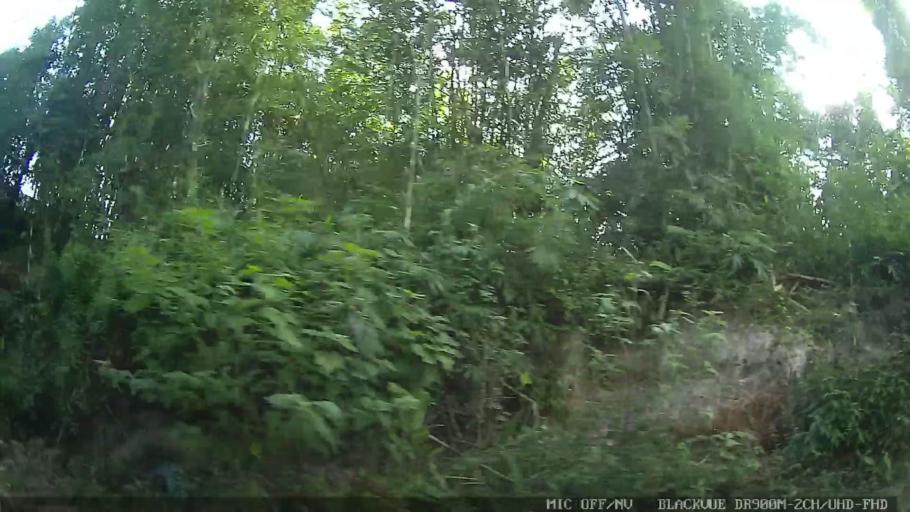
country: BR
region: Sao Paulo
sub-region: Itanhaem
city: Itanhaem
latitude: -24.1494
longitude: -46.8083
